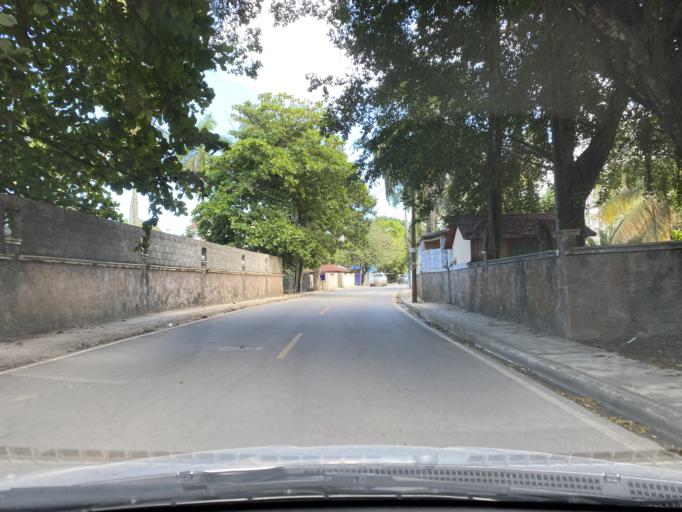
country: DO
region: Samana
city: Las Terrenas
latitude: 19.3080
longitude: -69.5482
